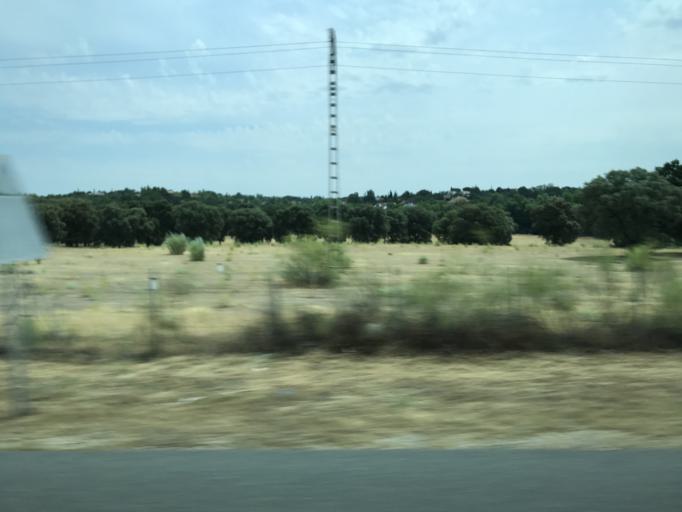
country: ES
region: Madrid
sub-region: Provincia de Madrid
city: San Agustin de Guadalix
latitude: 40.6342
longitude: -3.5903
